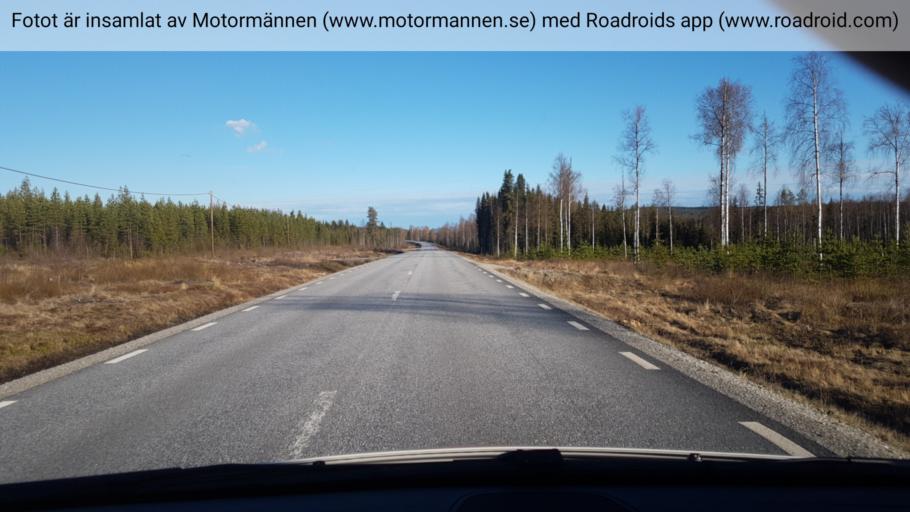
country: SE
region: Vaesterbotten
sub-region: Vindelns Kommun
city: Vindeln
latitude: 64.1934
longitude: 19.4584
